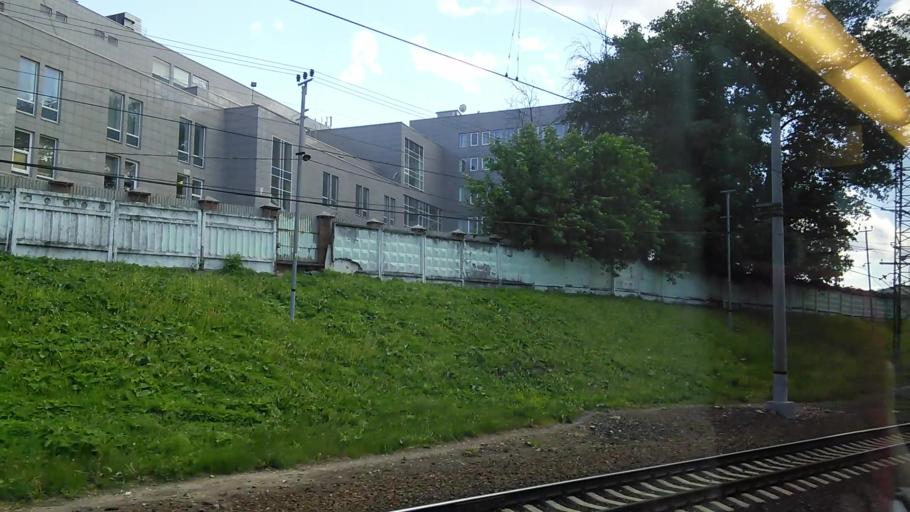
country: RU
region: Moskovskaya
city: Dorogomilovo
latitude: 55.7791
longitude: 37.5845
